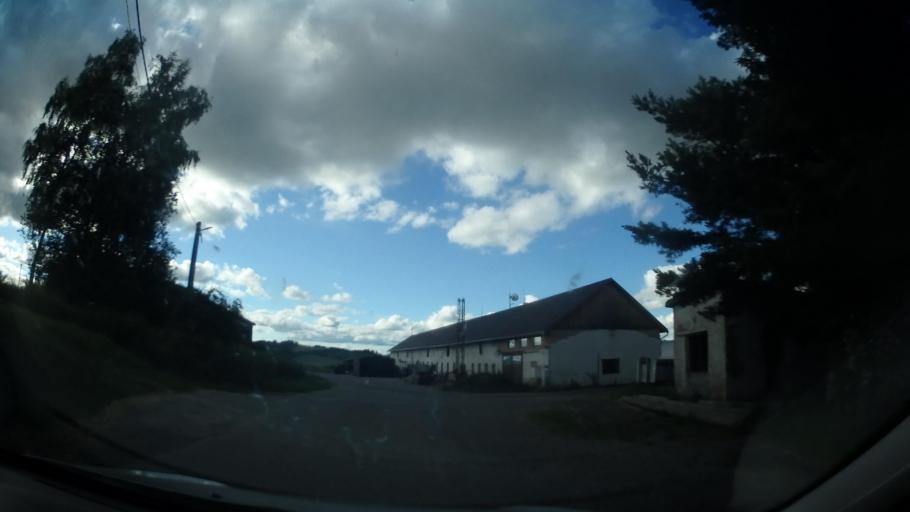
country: CZ
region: Vysocina
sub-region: Okres Zd'ar nad Sazavou
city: Jimramov
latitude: 49.6067
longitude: 16.1871
